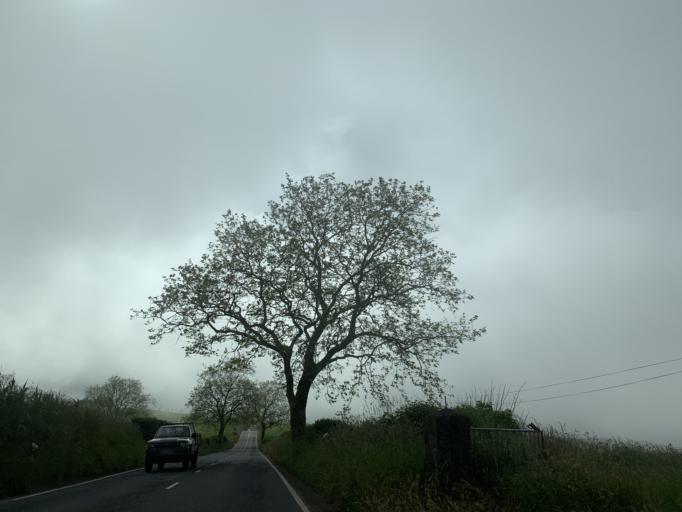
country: PT
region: Azores
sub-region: Ponta Delgada
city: Arrifes
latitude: 37.7741
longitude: -25.7450
